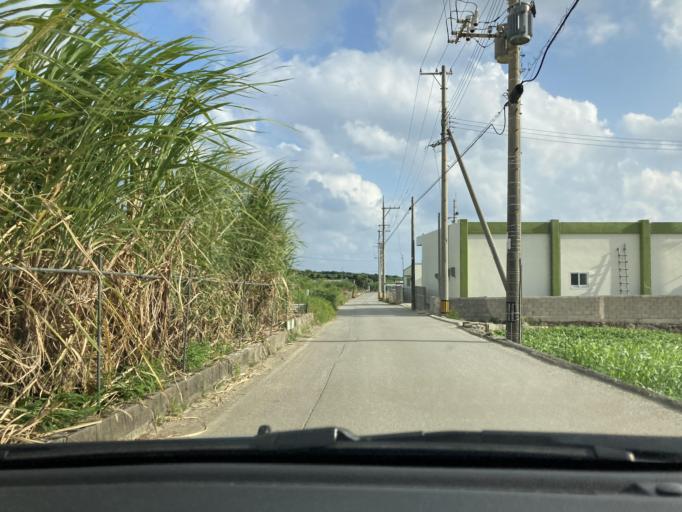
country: JP
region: Okinawa
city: Itoman
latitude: 26.0869
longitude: 127.6622
